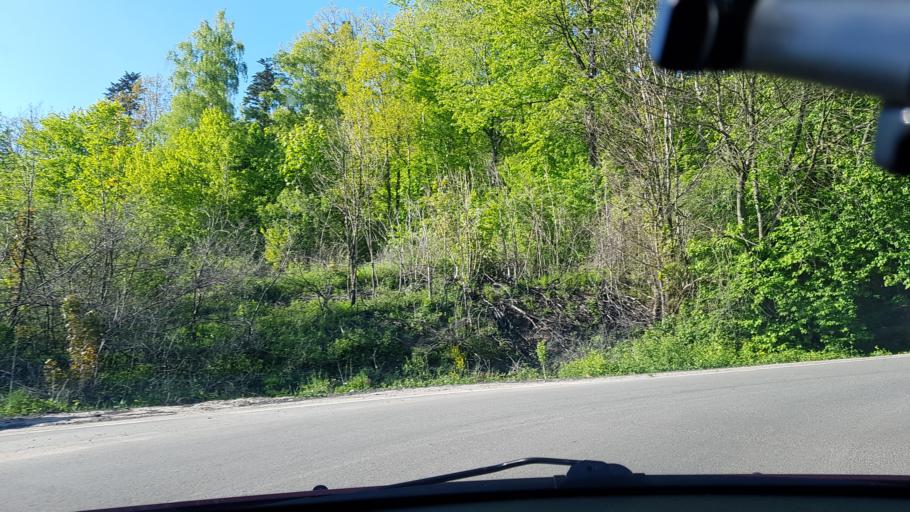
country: PL
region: Lower Silesian Voivodeship
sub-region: Powiat klodzki
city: Bozkow
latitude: 50.5709
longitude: 16.6226
